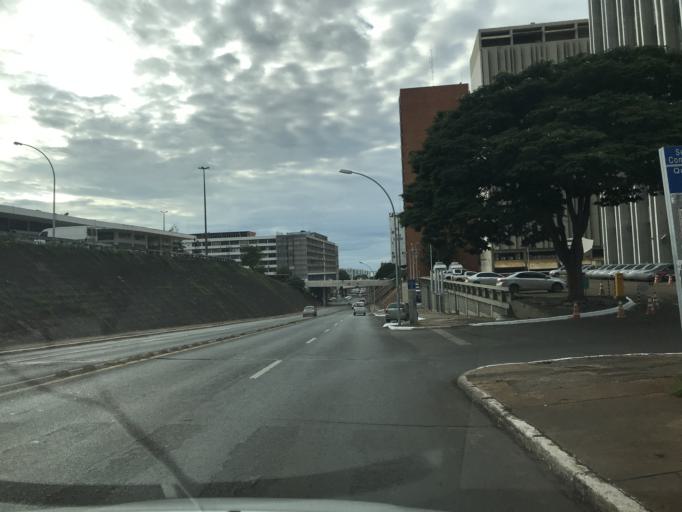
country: BR
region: Federal District
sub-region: Brasilia
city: Brasilia
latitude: -15.7963
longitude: -47.8876
